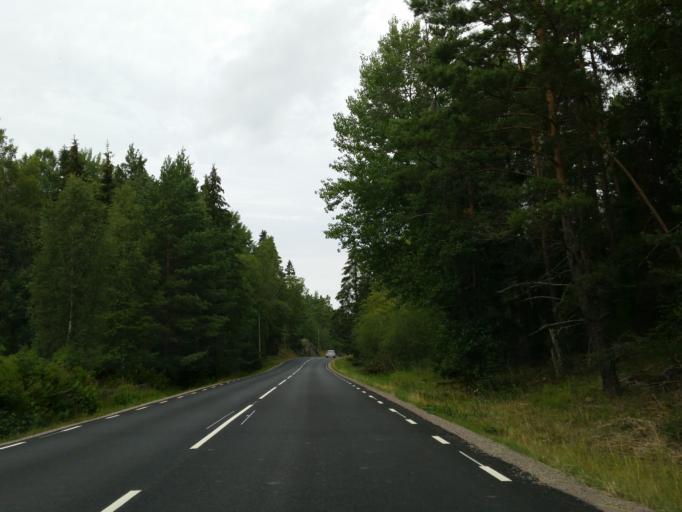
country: SE
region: Soedermanland
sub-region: Strangnas Kommun
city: Mariefred
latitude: 59.2660
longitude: 17.1609
